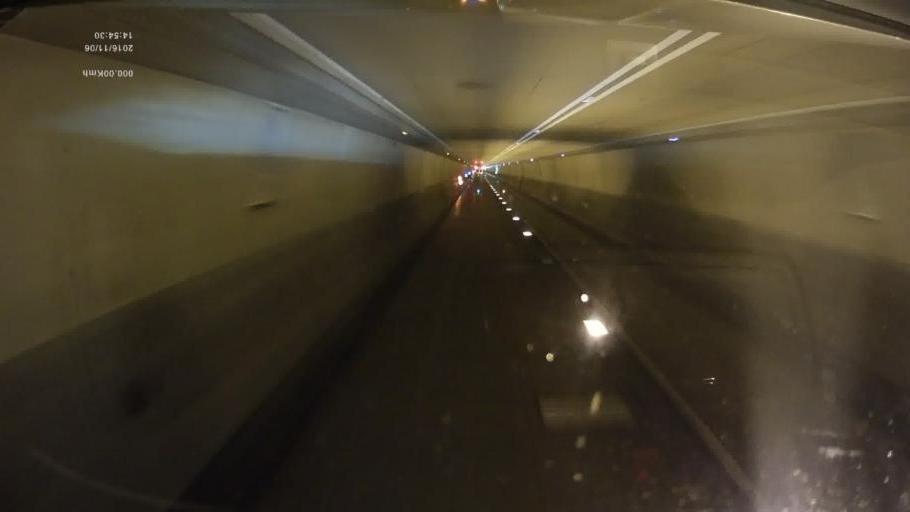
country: SK
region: Kosicky
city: Krompachy
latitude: 49.0032
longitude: 20.8769
